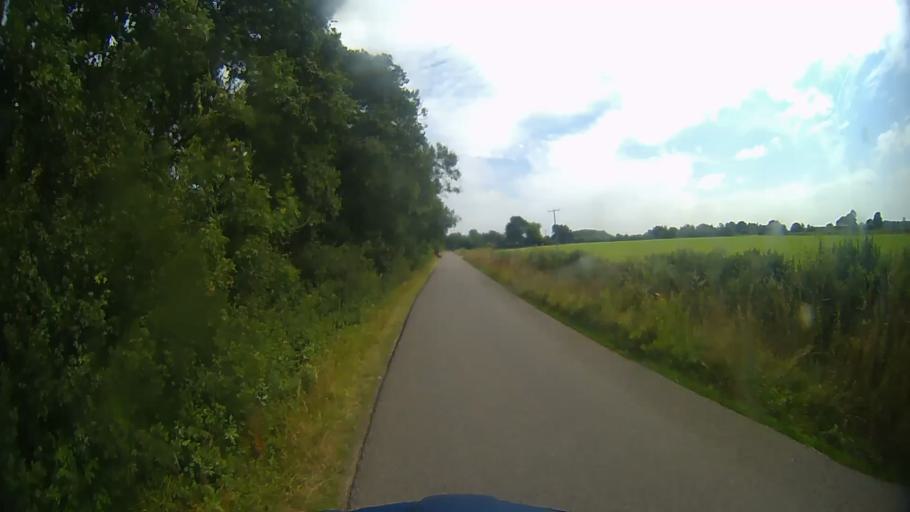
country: GB
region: England
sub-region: Hampshire
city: Lindford
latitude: 51.1516
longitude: -0.8447
